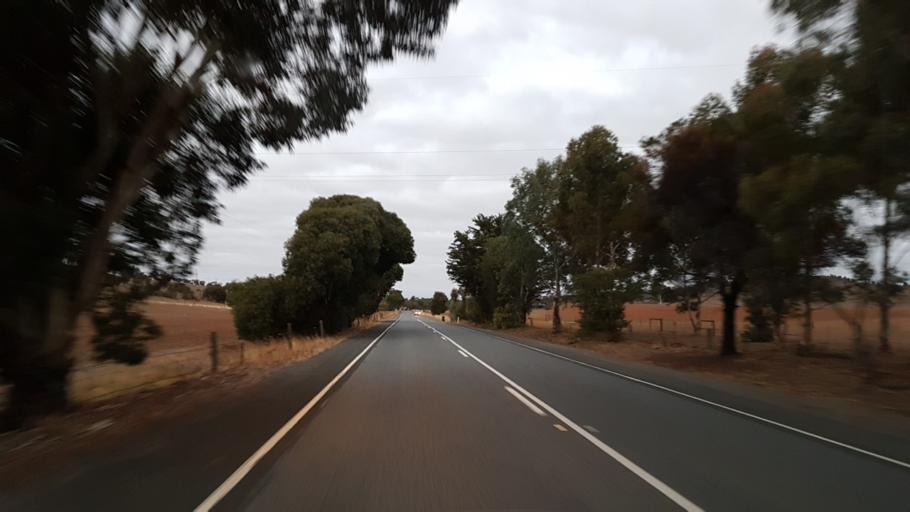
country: AU
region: South Australia
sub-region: Mount Barker
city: Callington
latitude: -35.0601
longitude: 139.0119
